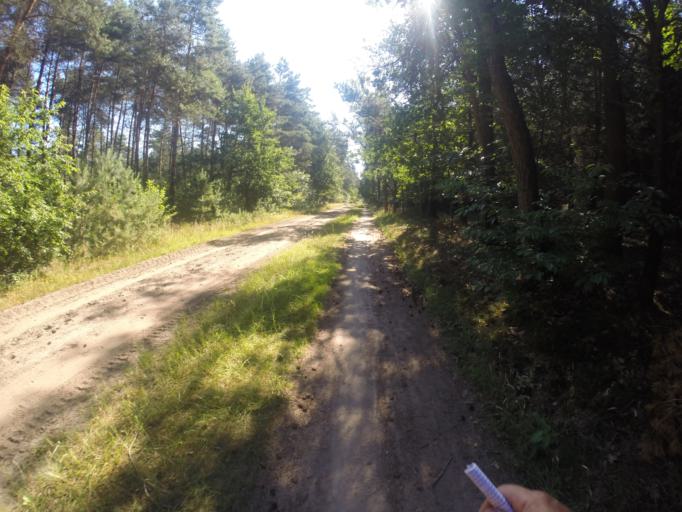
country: NL
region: Gelderland
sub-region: Gemeente Lochem
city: Almen
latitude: 52.1298
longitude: 6.3508
